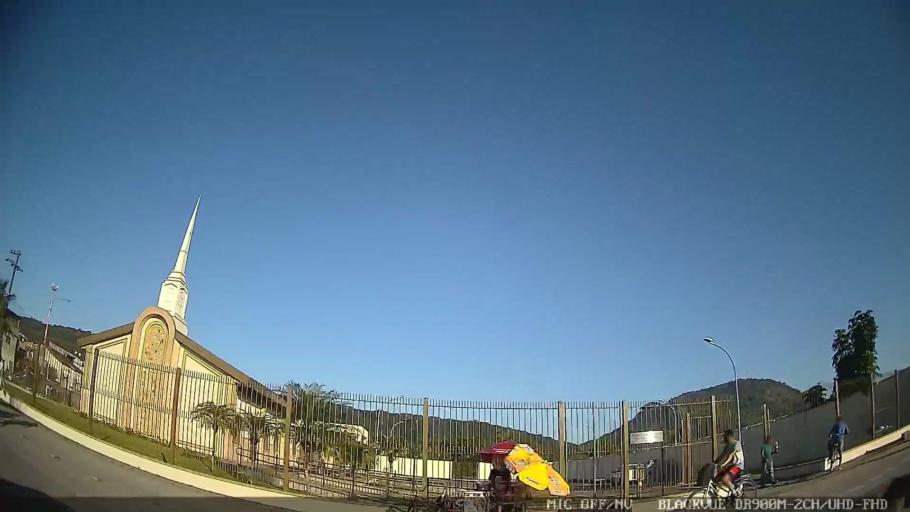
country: BR
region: Sao Paulo
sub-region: Guaruja
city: Guaruja
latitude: -23.9647
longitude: -46.2504
